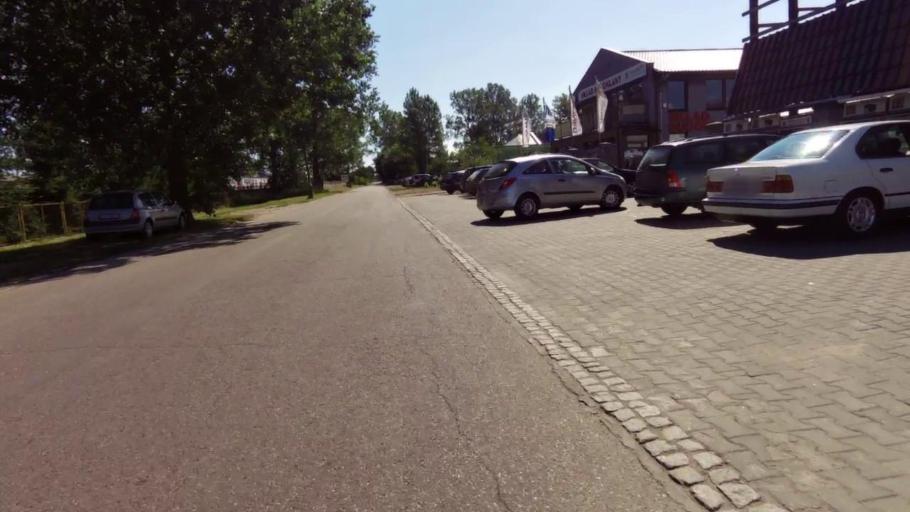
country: PL
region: West Pomeranian Voivodeship
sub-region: Powiat drawski
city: Zlocieniec
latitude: 53.5256
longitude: 16.0207
